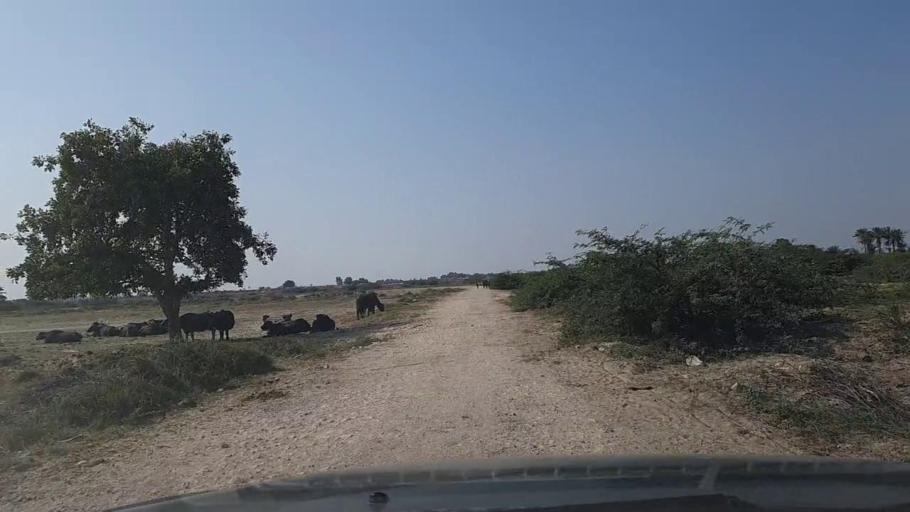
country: PK
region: Sindh
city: Mirpur Sakro
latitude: 24.4061
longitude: 67.6745
